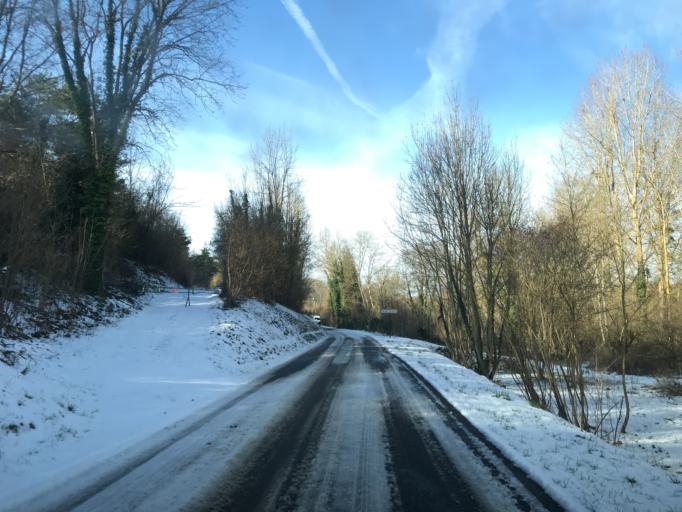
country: FR
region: Haute-Normandie
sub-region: Departement de l'Eure
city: Saint-Aubin-sur-Gaillon
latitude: 49.0810
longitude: 1.2786
